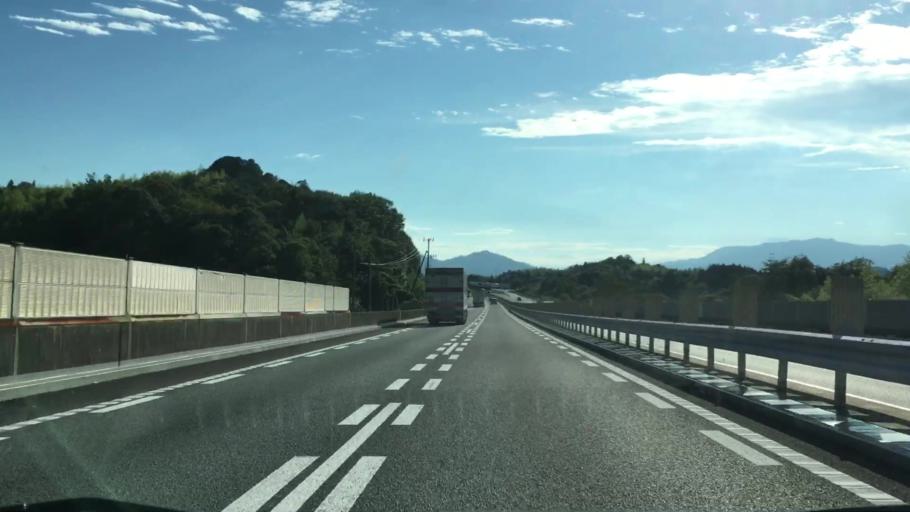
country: JP
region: Yamaguchi
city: Iwakuni
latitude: 34.1025
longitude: 132.1077
